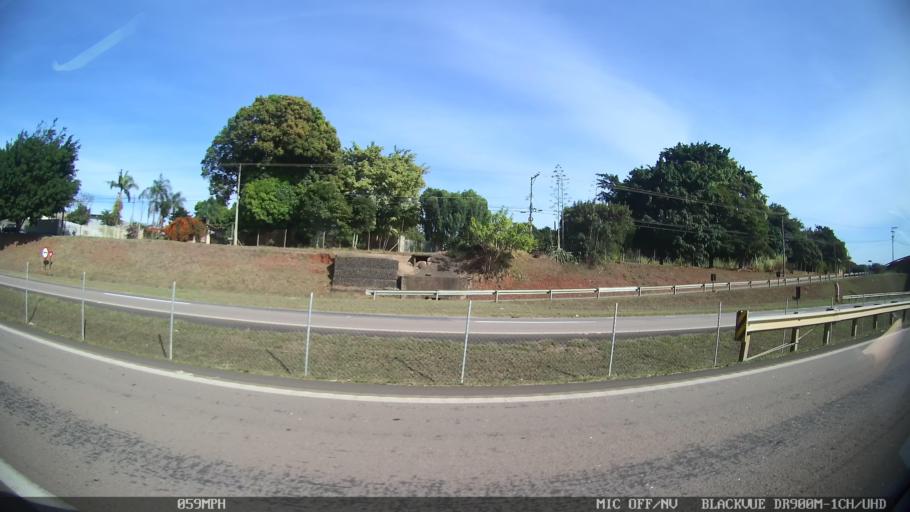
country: BR
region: Sao Paulo
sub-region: Piracicaba
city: Piracicaba
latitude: -22.7656
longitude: -47.5953
